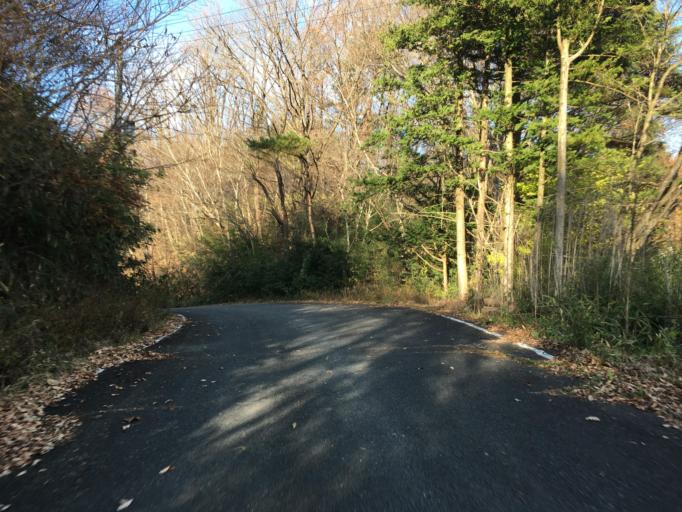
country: JP
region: Fukushima
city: Ishikawa
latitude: 37.2560
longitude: 140.5696
